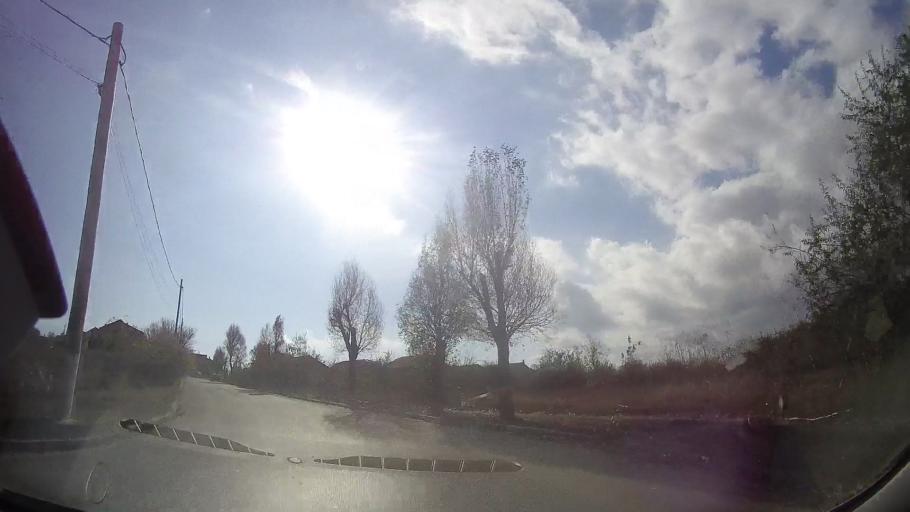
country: RO
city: Eforie Sud
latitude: 44.0177
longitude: 28.6471
